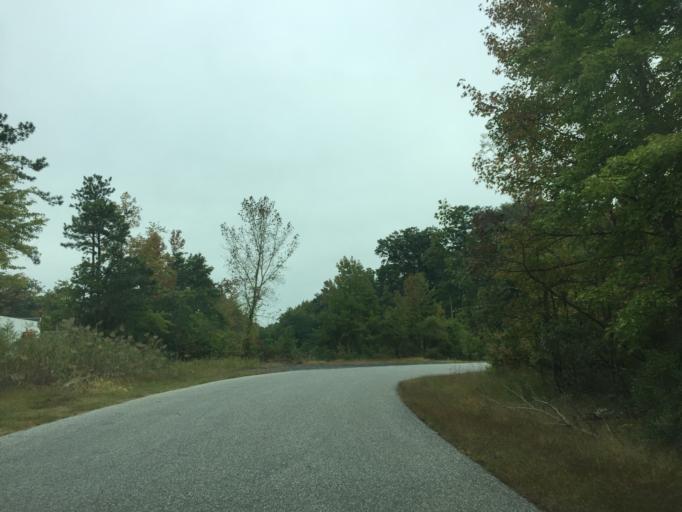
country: US
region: Maryland
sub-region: Baltimore County
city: Bowleys Quarters
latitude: 39.3494
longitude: -76.4035
